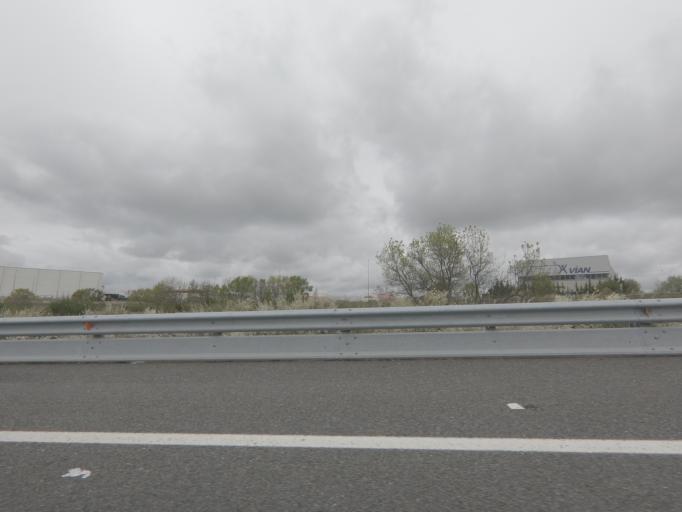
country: ES
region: Castille and Leon
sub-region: Provincia de Salamanca
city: Bejar
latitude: 40.3929
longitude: -5.7897
